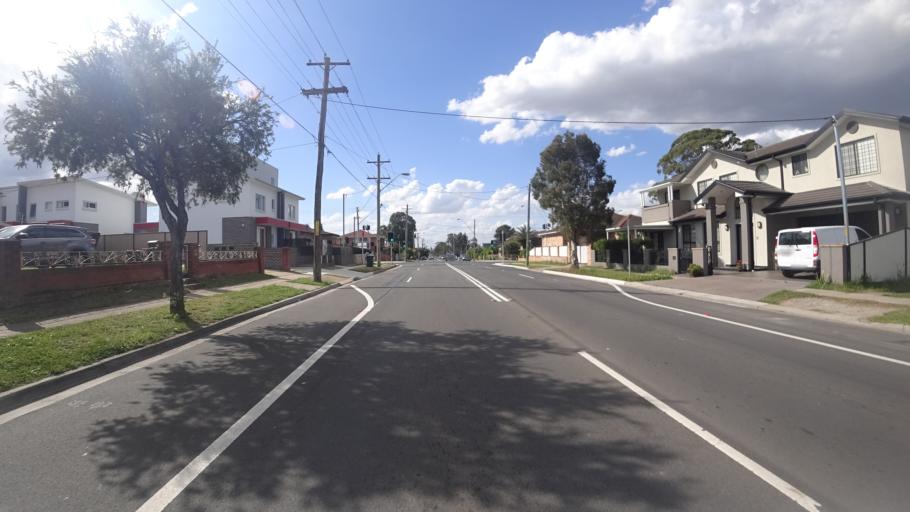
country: AU
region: New South Wales
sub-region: Liverpool
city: Miller
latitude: -33.9236
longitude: 150.9081
